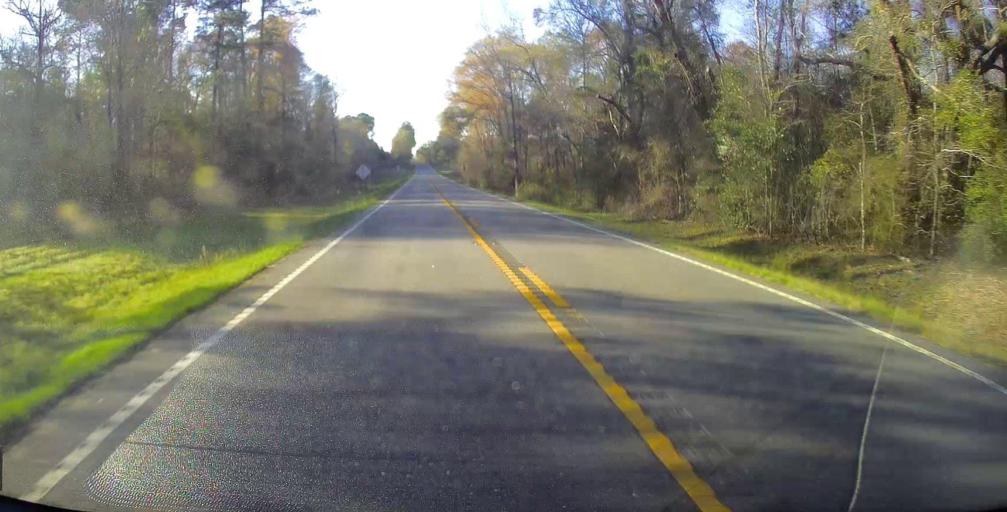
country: US
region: Georgia
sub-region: Pulaski County
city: Hawkinsville
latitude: 32.2369
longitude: -83.4003
